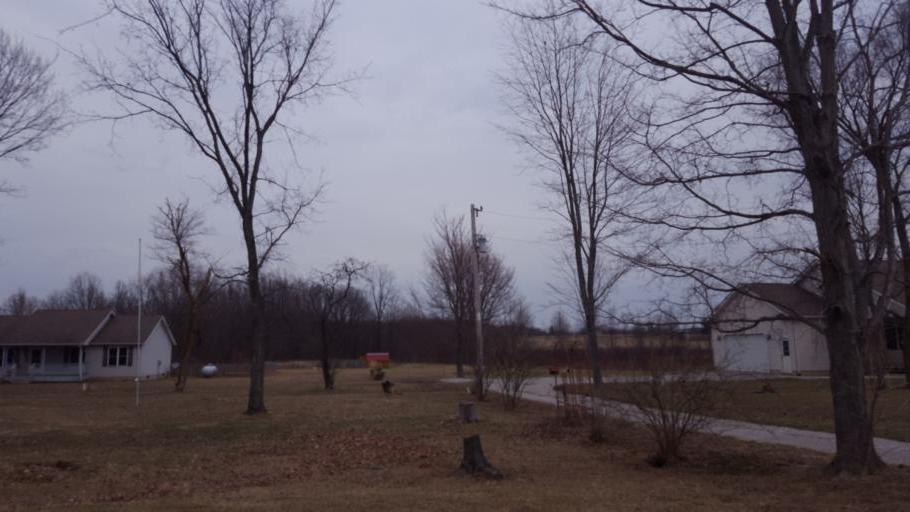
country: US
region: Ohio
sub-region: Morrow County
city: Mount Gilead
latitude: 40.6284
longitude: -82.7920
